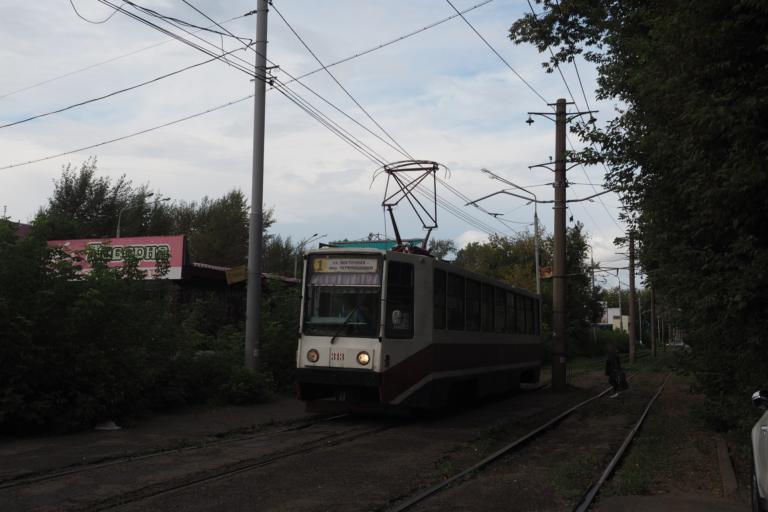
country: RU
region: Tomsk
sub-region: Tomskiy Rayon
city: Tomsk
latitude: 56.4718
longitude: 84.9822
